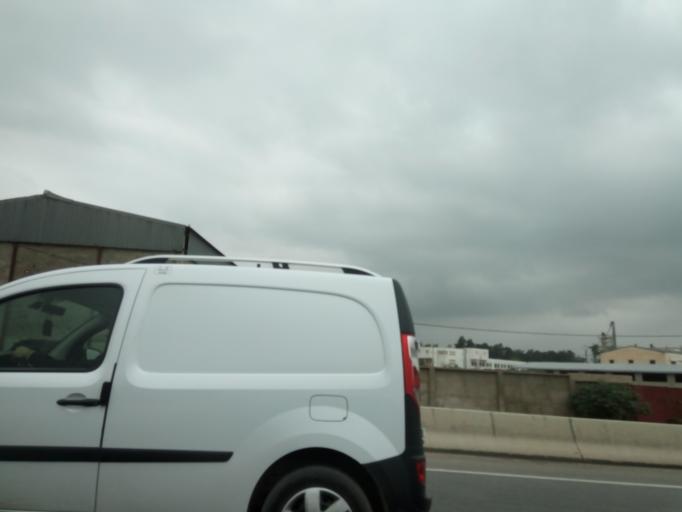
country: DZ
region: Blida
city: Chiffa
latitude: 36.4449
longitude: 2.7507
